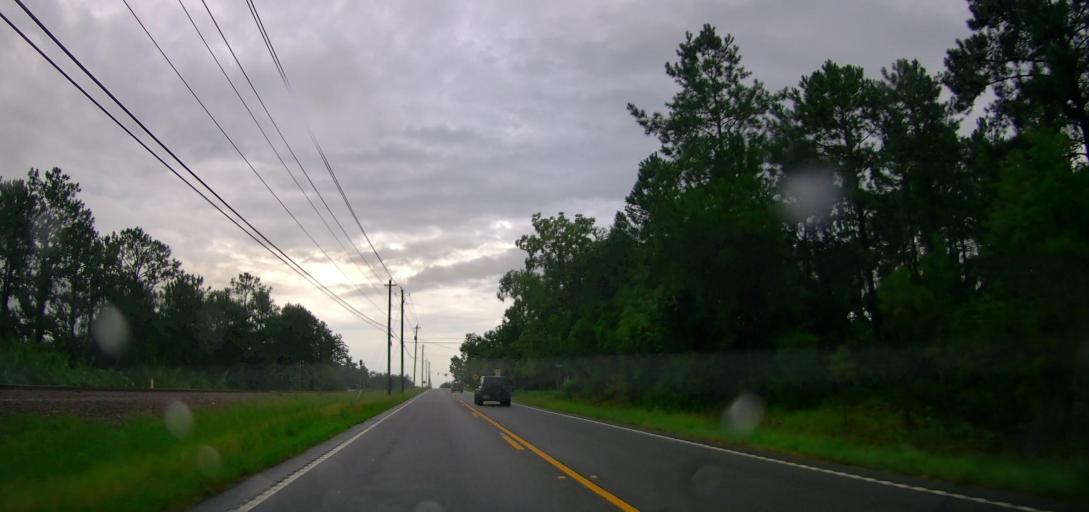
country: US
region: Georgia
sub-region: Ware County
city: Deenwood
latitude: 31.2539
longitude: -82.3770
